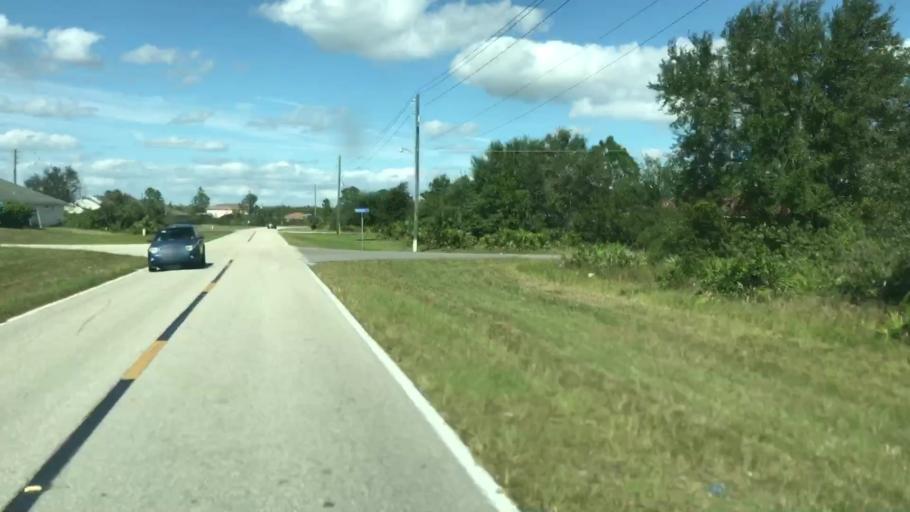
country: US
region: Florida
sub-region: Lee County
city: Lehigh Acres
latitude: 26.6716
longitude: -81.6258
